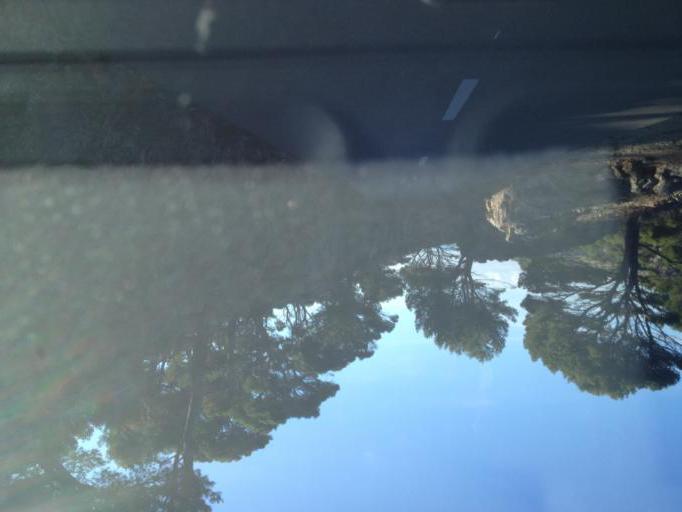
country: ES
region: Balearic Islands
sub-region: Illes Balears
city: Alcudia
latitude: 39.9534
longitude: 3.2018
